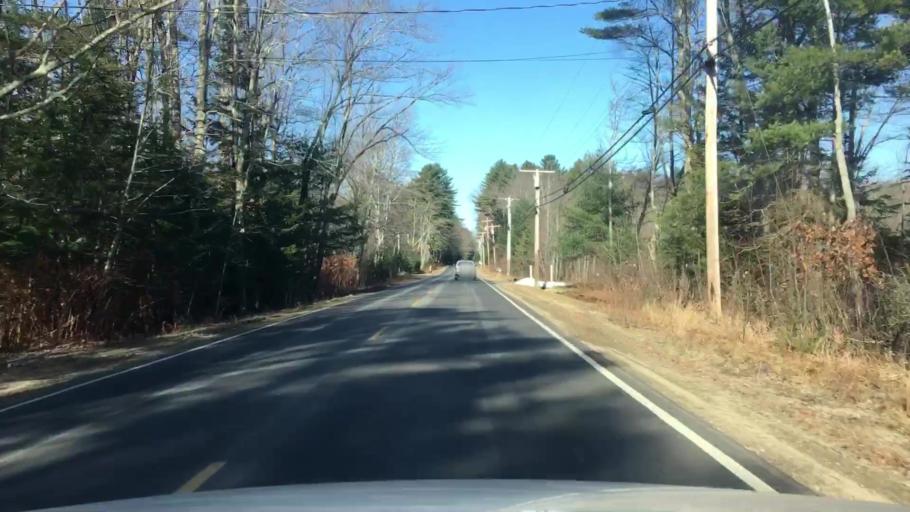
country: US
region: Maine
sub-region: York County
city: Arundel
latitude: 43.3880
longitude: -70.4804
